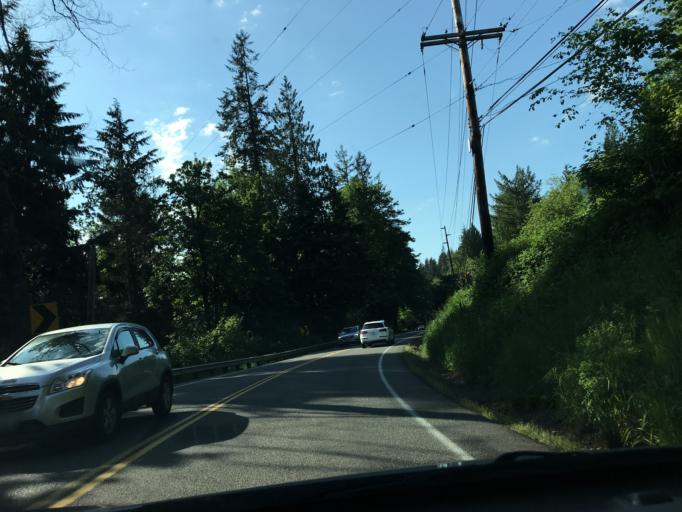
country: US
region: Washington
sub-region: King County
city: Mirrormont
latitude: 47.4547
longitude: -121.9992
